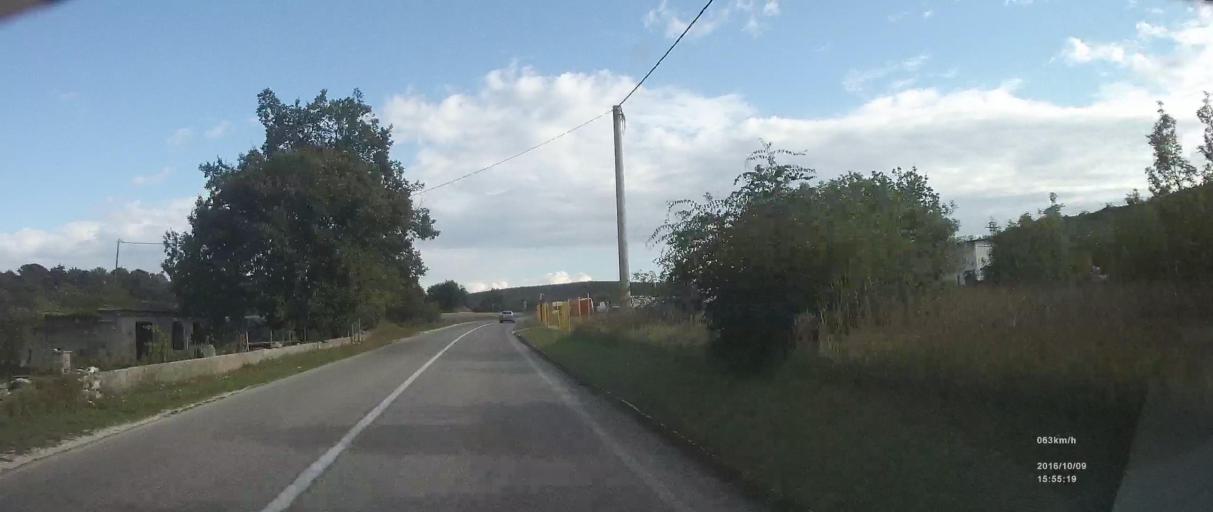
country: HR
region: Splitsko-Dalmatinska
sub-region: Grad Trogir
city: Trogir
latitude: 43.5878
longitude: 16.2297
